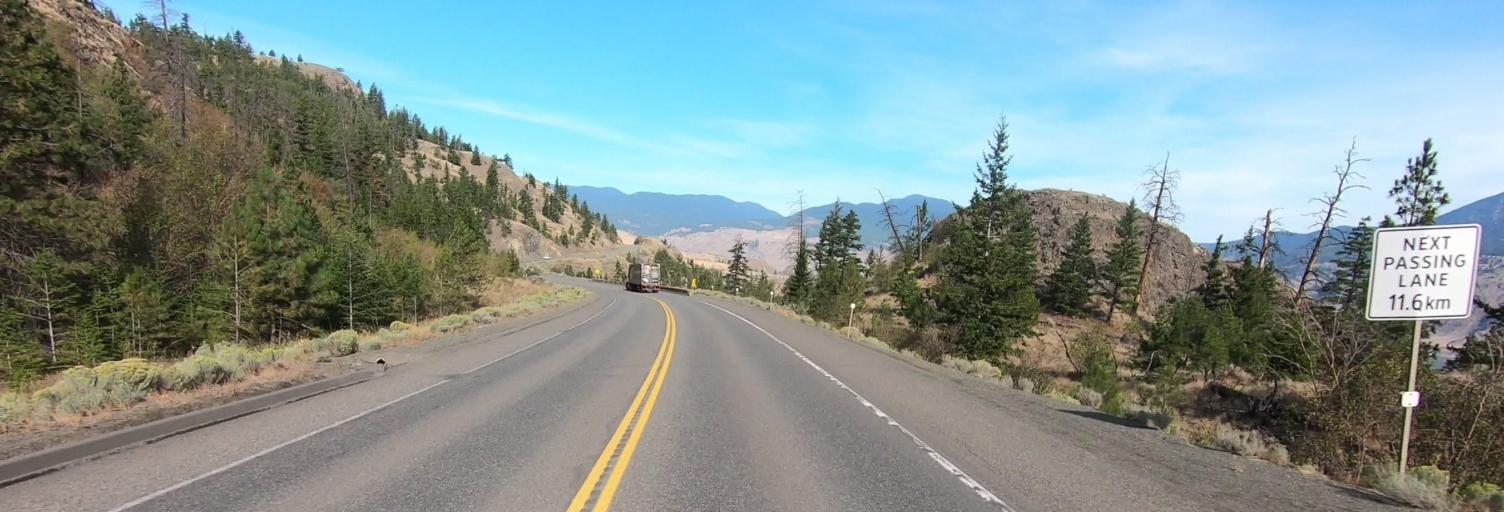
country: CA
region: British Columbia
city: Logan Lake
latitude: 50.7529
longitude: -120.7297
